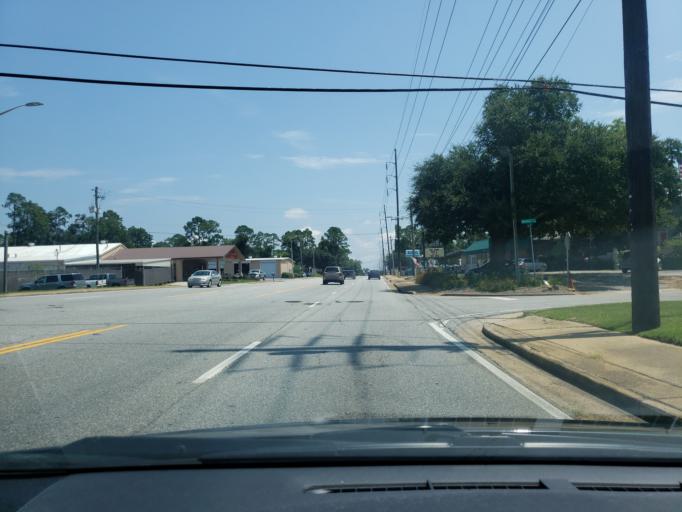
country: US
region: Georgia
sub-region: Dougherty County
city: Albany
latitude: 31.5811
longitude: -84.1873
